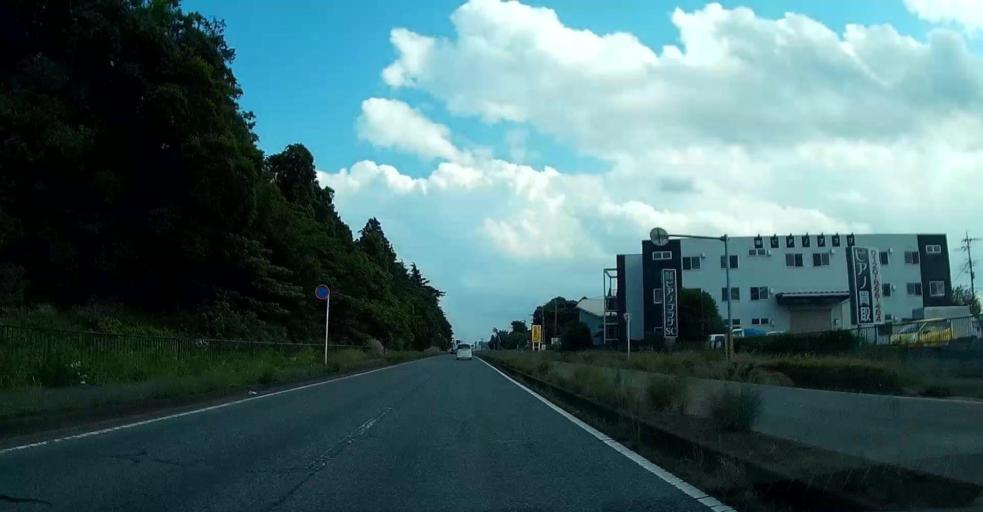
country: JP
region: Chiba
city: Noda
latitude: 35.9669
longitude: 139.8679
